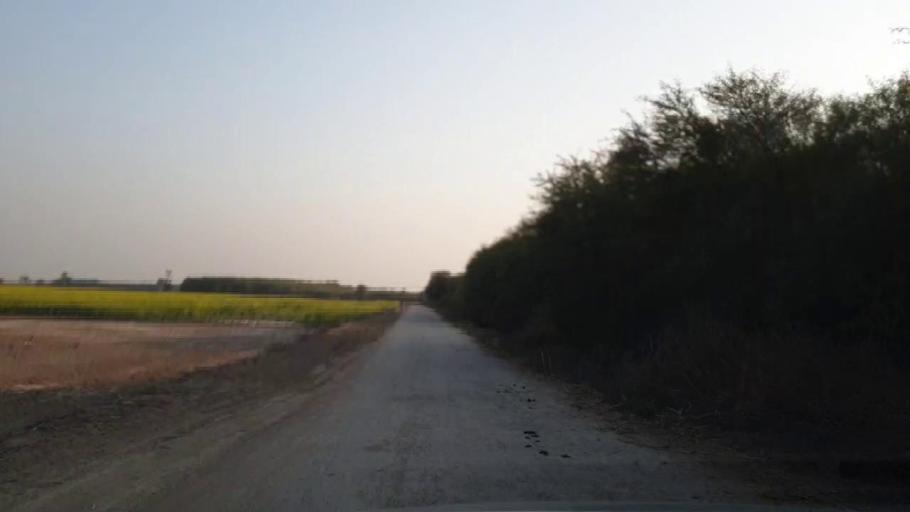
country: PK
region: Sindh
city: Tando Adam
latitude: 25.7165
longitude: 68.5942
